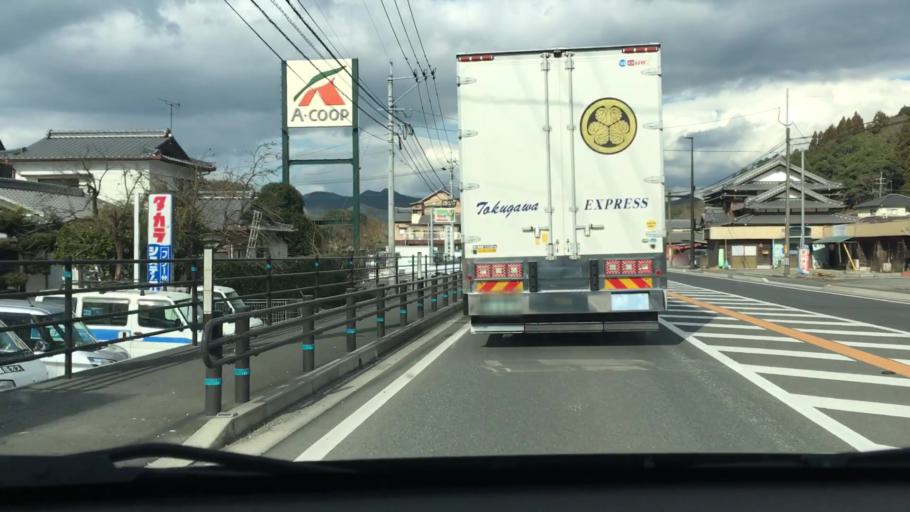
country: JP
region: Oita
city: Usuki
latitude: 33.0372
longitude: 131.6895
